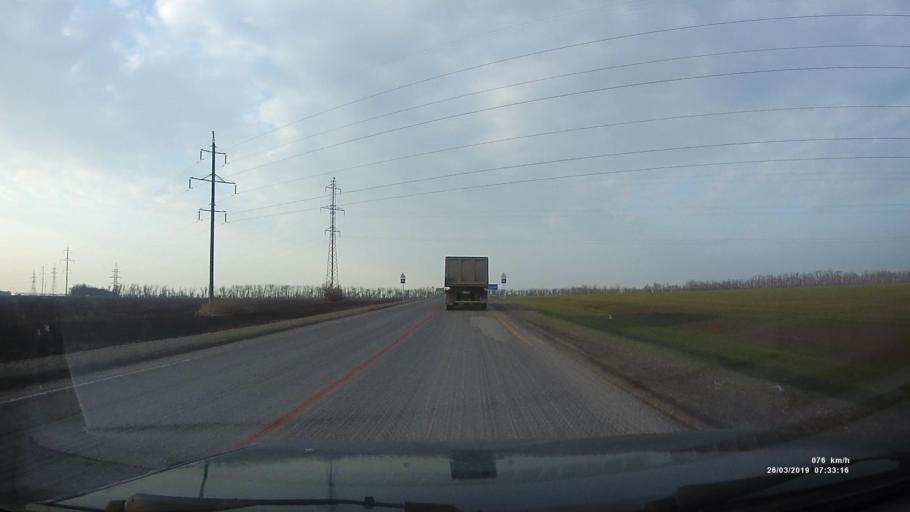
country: RU
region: Rostov
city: Novobessergenovka
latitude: 47.2175
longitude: 38.7714
